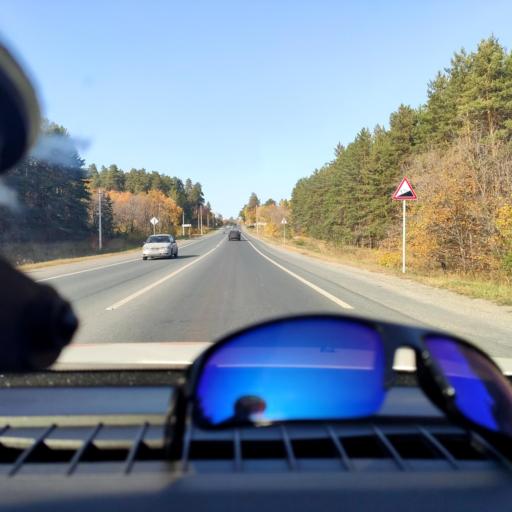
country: RU
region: Samara
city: Volzhskiy
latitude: 53.4411
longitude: 50.1238
